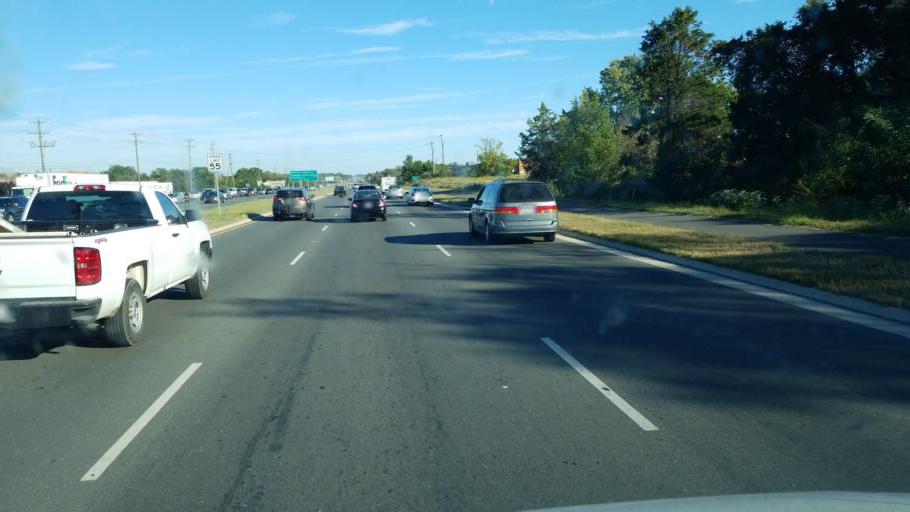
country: US
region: Virginia
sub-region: Loudoun County
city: South Riding
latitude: 38.9120
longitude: -77.4755
